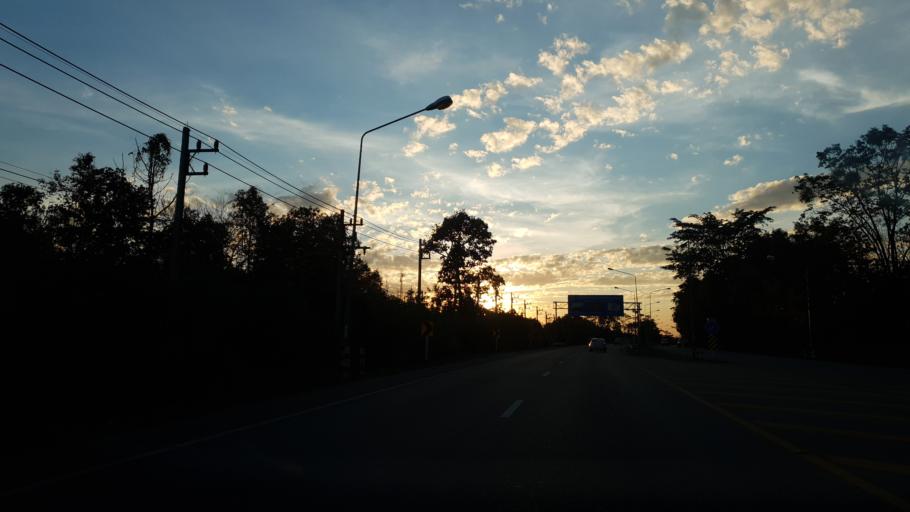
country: TH
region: Phitsanulok
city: Nakhon Thai
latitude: 16.8576
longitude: 100.7438
